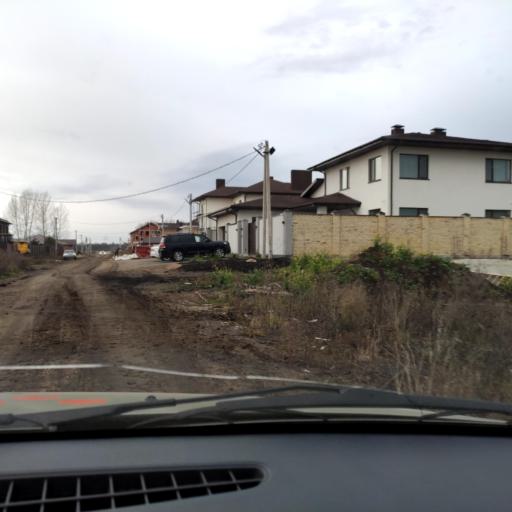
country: RU
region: Bashkortostan
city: Ufa
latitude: 54.6610
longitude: 55.9223
